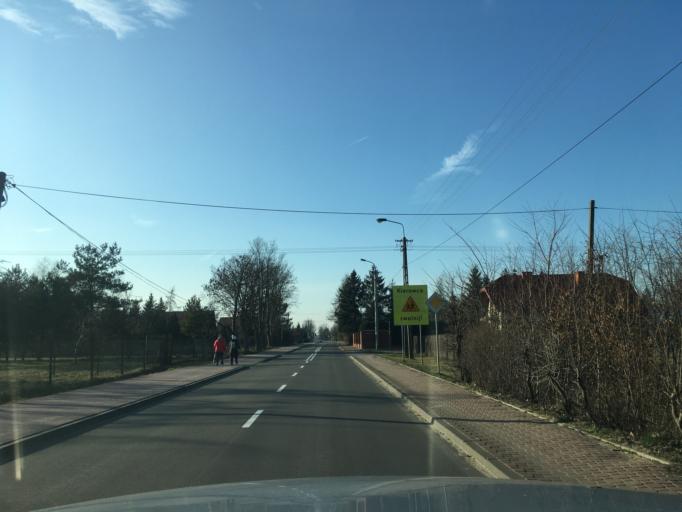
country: PL
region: Masovian Voivodeship
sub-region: Powiat pruszkowski
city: Nadarzyn
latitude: 52.0489
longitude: 20.7769
